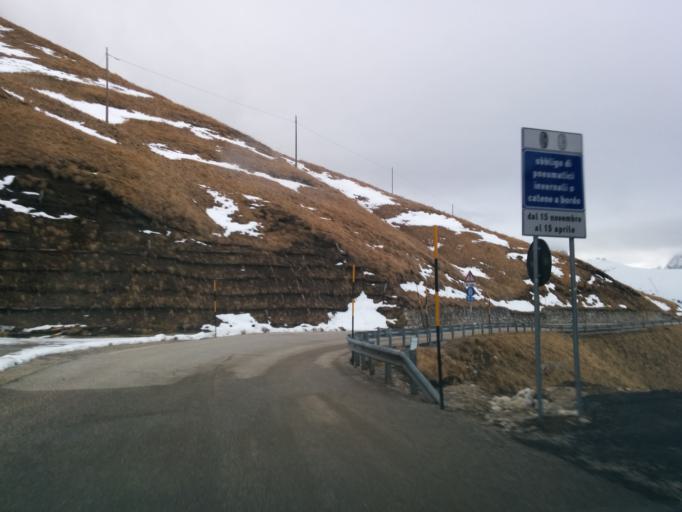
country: IT
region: Trentino-Alto Adige
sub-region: Provincia di Trento
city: Canazei
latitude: 46.5079
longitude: 11.7689
